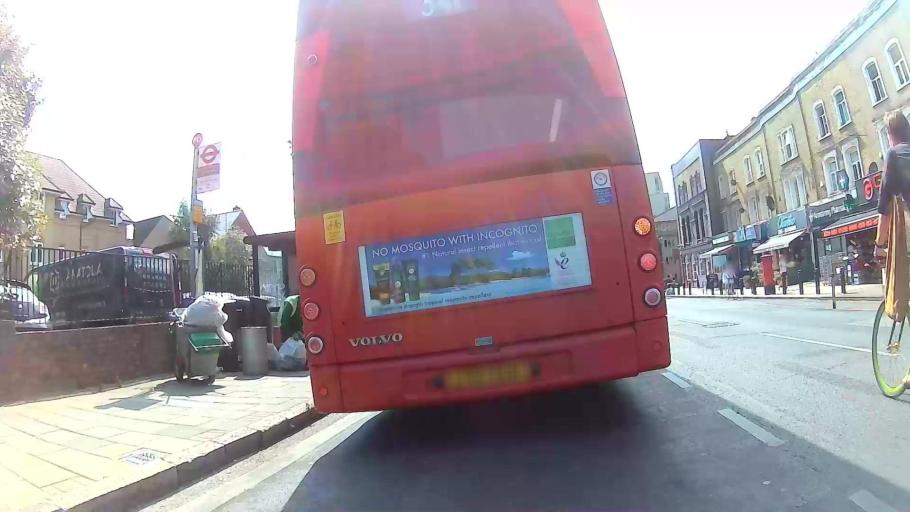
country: GB
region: England
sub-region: Greater London
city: Harringay
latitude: 51.5645
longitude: -0.0928
